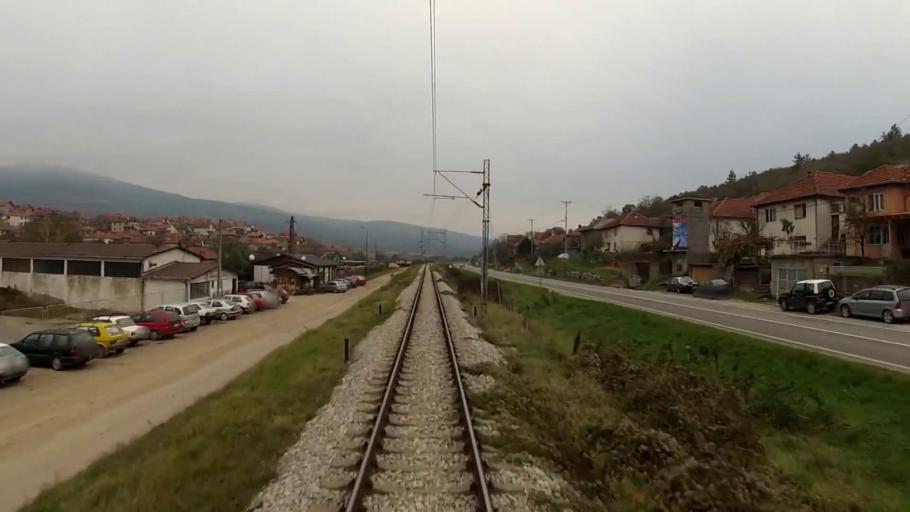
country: RS
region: Central Serbia
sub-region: Pirotski Okrug
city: Dimitrovgrad
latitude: 43.0148
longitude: 22.7939
